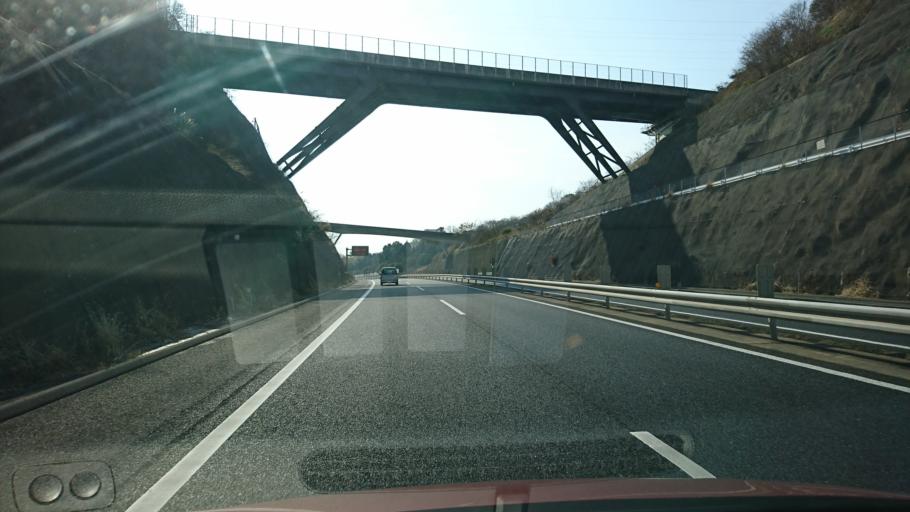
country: JP
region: Hiroshima
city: Onomichi
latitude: 34.4225
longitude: 133.2188
